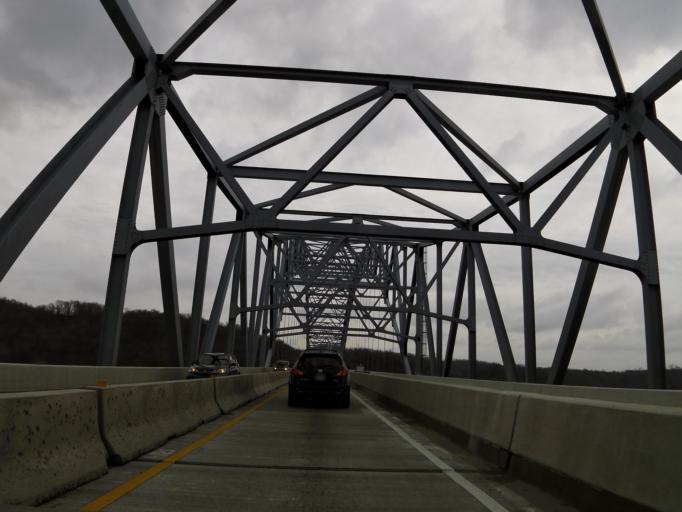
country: US
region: Indiana
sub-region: Dearborn County
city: Lawrenceburg
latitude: 39.1048
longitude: -84.8266
